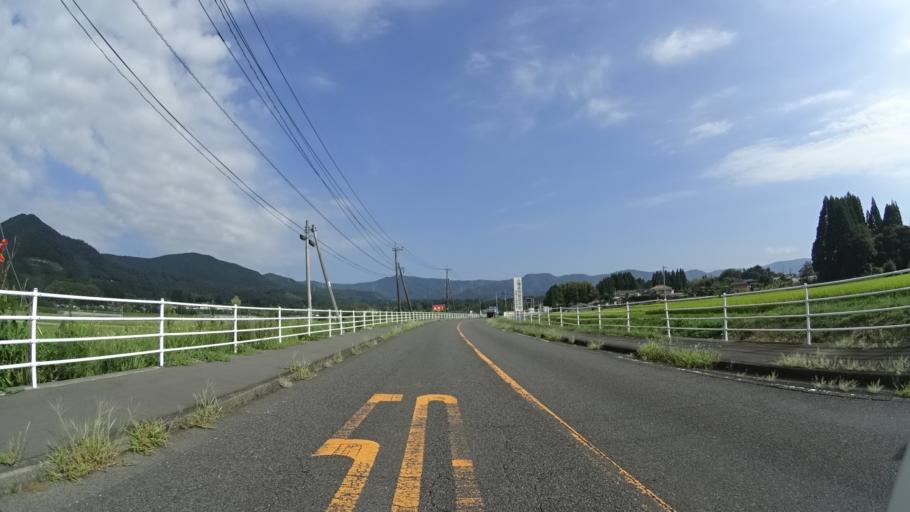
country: JP
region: Kagoshima
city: Okuchi-shinohara
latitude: 32.0314
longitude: 130.7435
